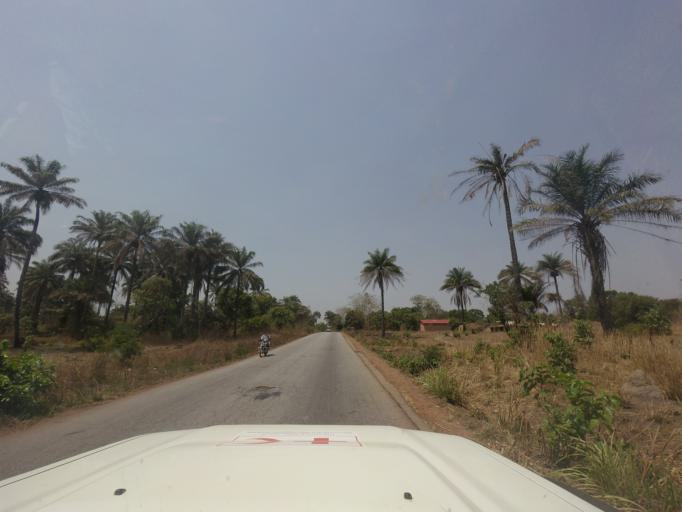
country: GN
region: Kindia
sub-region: Kindia
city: Kindia
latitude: 9.9374
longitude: -12.9785
